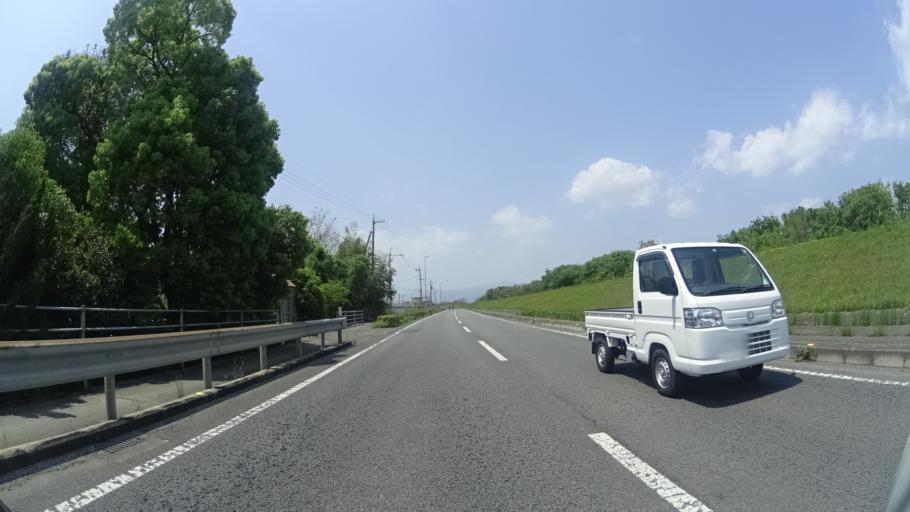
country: JP
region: Tokushima
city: Kamojimacho-jogejima
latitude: 34.0616
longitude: 134.2938
